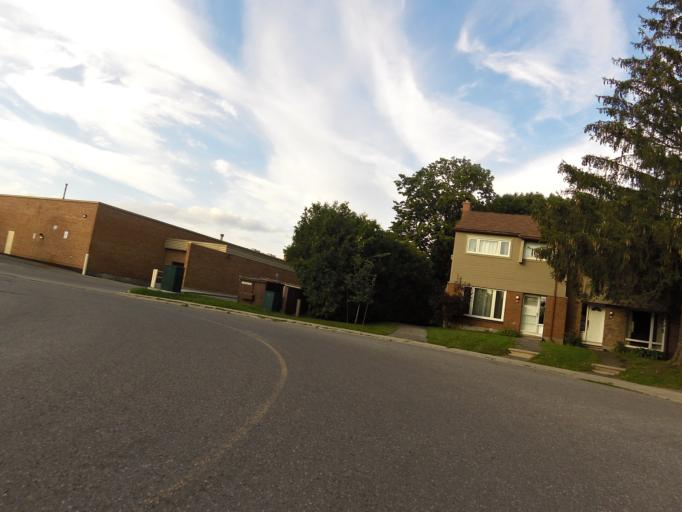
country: CA
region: Ontario
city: Bells Corners
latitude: 45.3235
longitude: -75.7804
